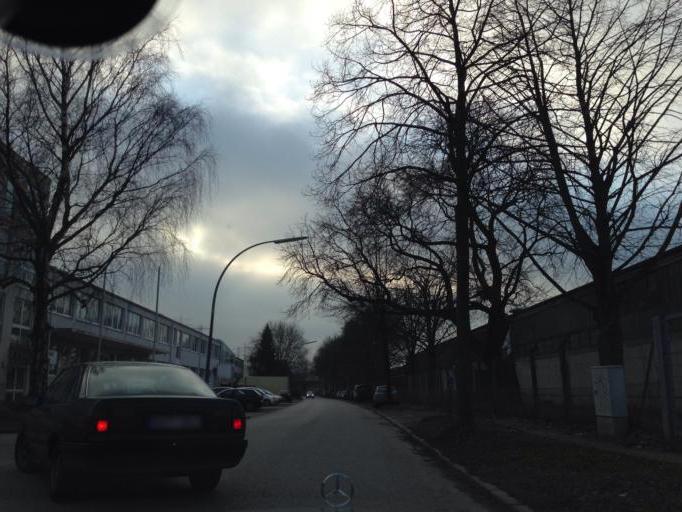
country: DE
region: Hamburg
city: Wandsbek
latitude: 53.5786
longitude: 10.1129
